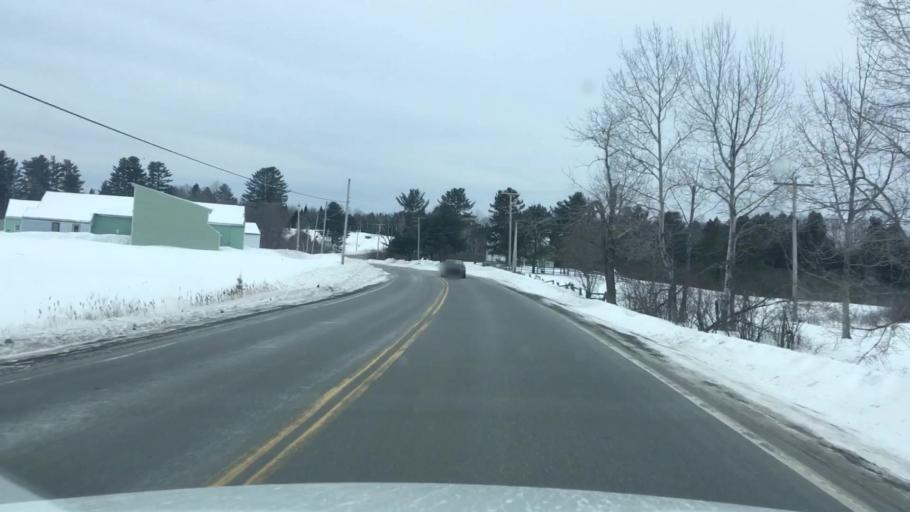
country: US
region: Maine
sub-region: Penobscot County
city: Charleston
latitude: 44.9991
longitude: -69.0351
